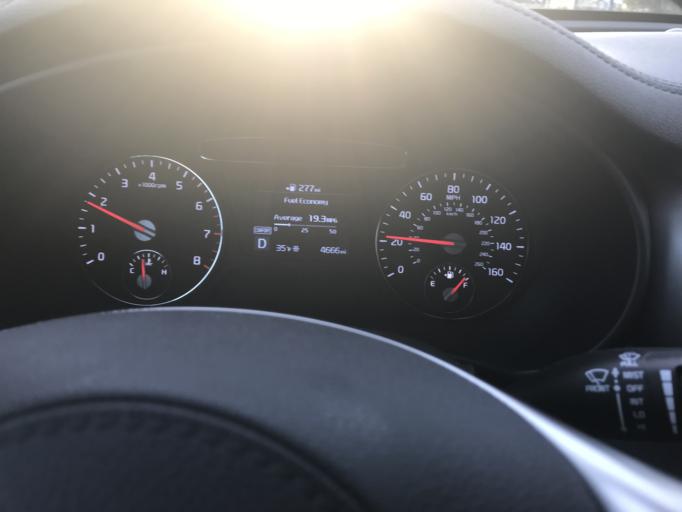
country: US
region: Georgia
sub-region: Cobb County
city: Mableton
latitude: 33.7823
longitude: -84.5389
